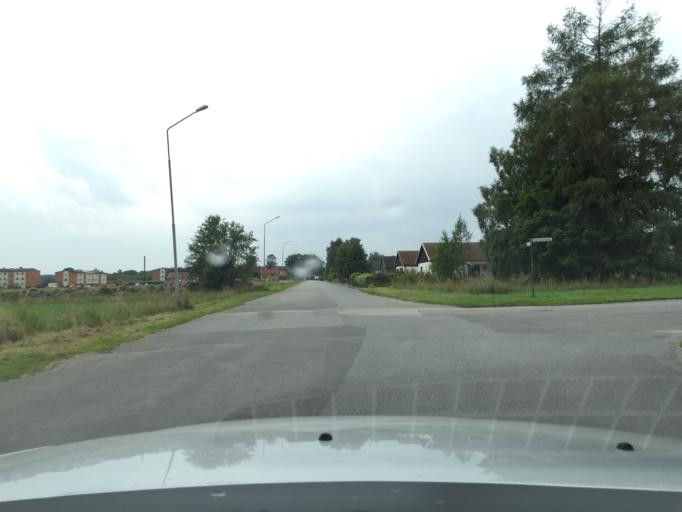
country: SE
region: Skane
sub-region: Hassleholms Kommun
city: Sosdala
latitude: 56.0360
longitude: 13.6841
